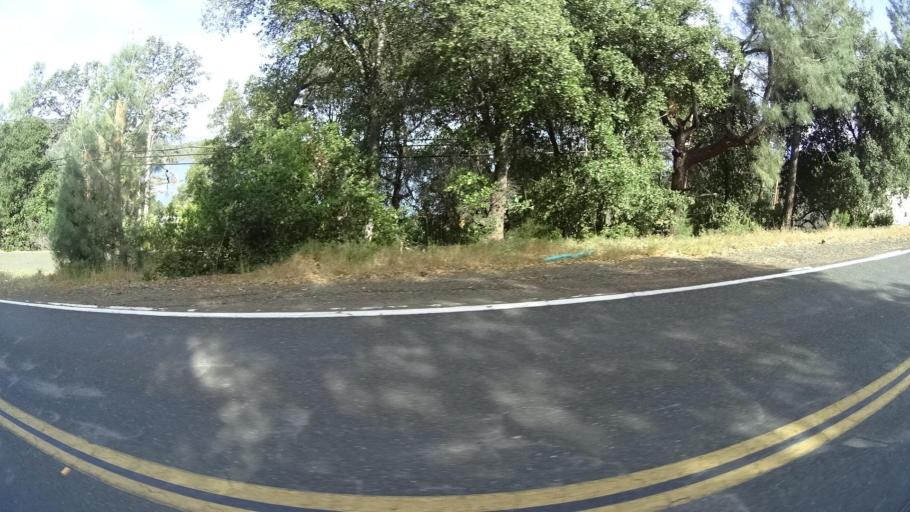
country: US
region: California
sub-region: Lake County
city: Soda Bay
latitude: 39.0087
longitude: -122.7786
